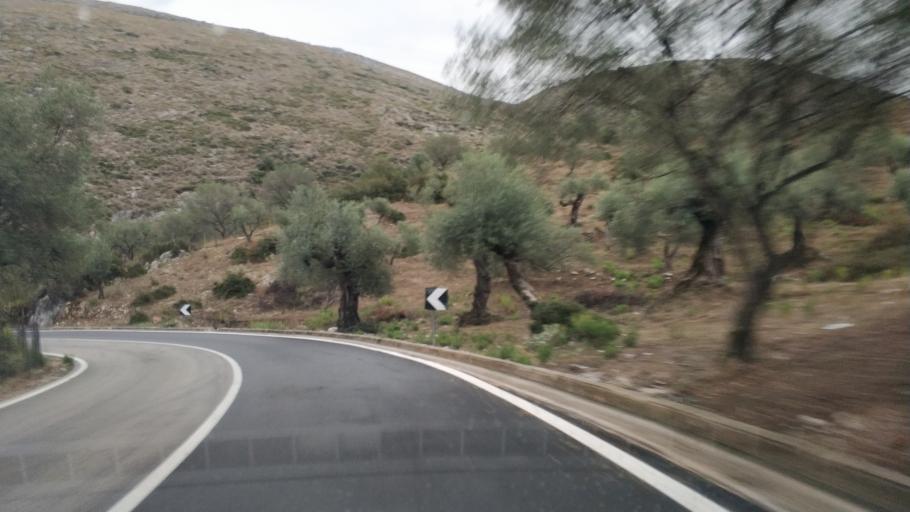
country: AL
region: Vlore
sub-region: Rrethi i Sarandes
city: Lukove
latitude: 39.9641
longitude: 19.9629
